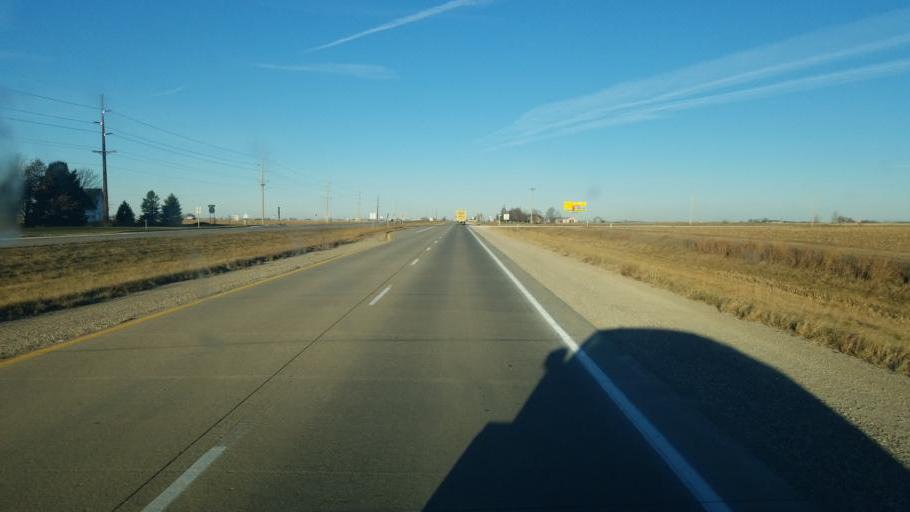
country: US
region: Iowa
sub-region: Marion County
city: Pella
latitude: 41.3630
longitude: -92.7830
